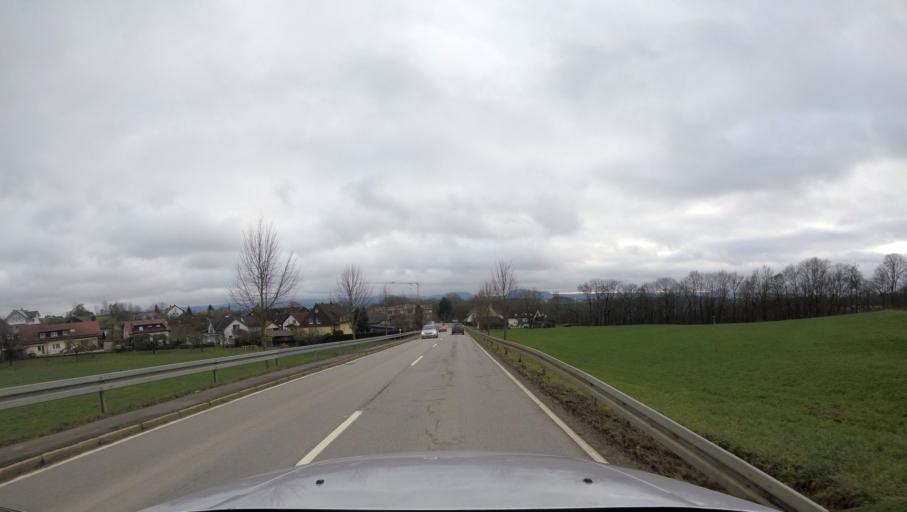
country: DE
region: Baden-Wuerttemberg
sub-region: Regierungsbezirk Stuttgart
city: Durlangen
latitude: 48.8423
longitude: 9.7701
